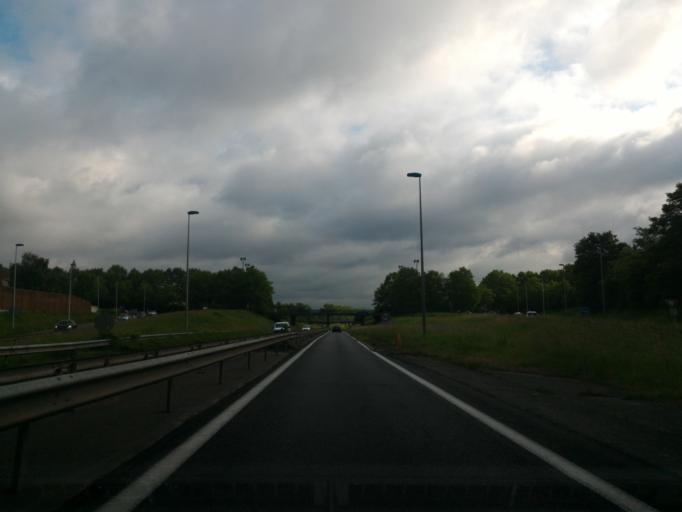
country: FR
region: Ile-de-France
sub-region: Departement de Seine-et-Marne
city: Lognes
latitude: 48.8374
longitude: 2.6243
